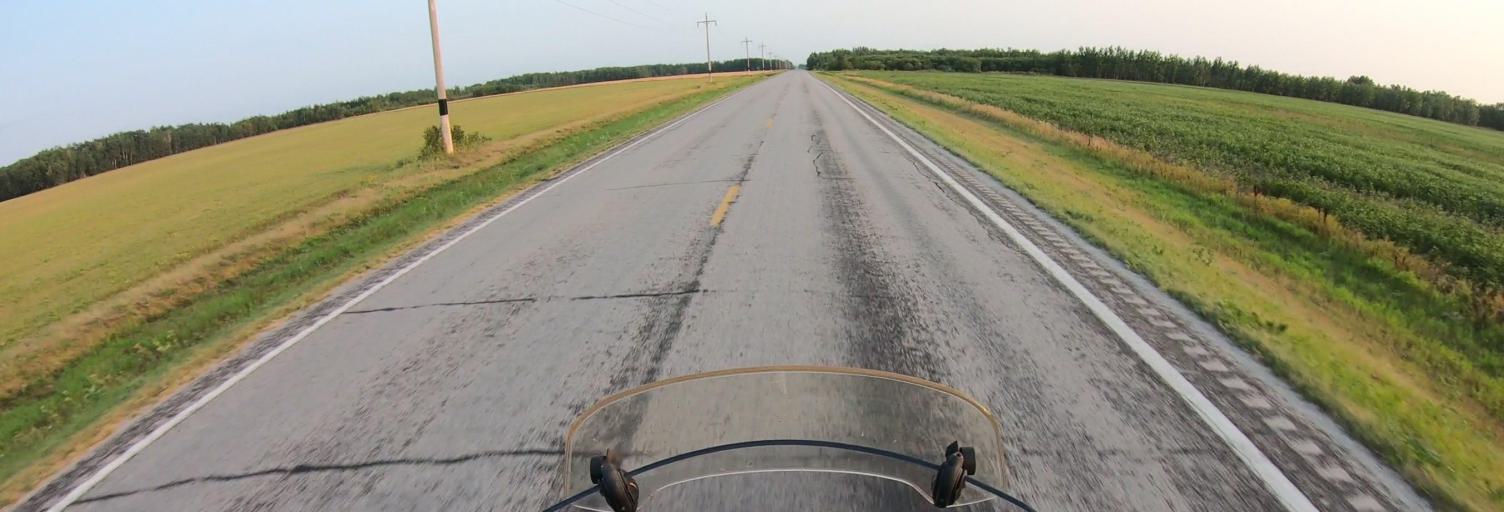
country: US
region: Minnesota
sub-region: Roseau County
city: Warroad
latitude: 48.8137
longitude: -95.3306
